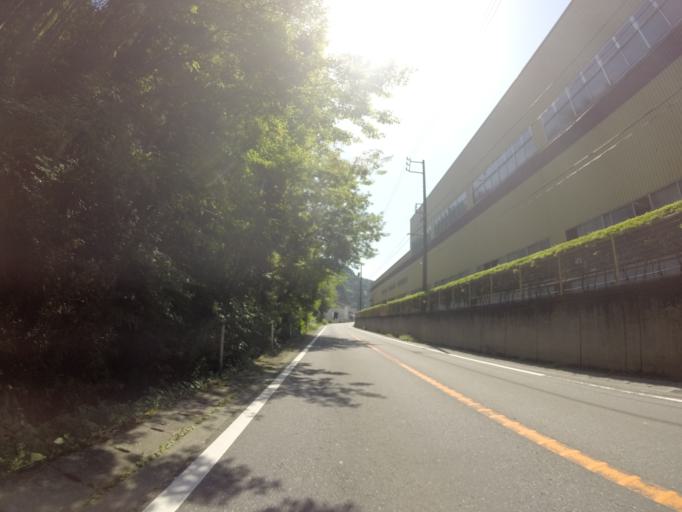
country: JP
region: Shizuoka
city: Fujinomiya
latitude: 35.1926
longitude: 138.5761
